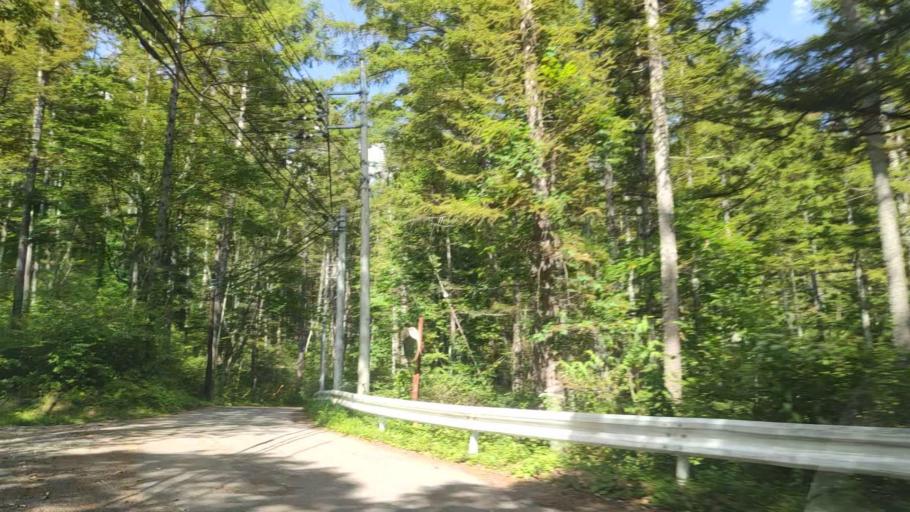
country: JP
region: Gunma
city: Nakanojomachi
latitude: 36.6599
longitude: 138.6238
